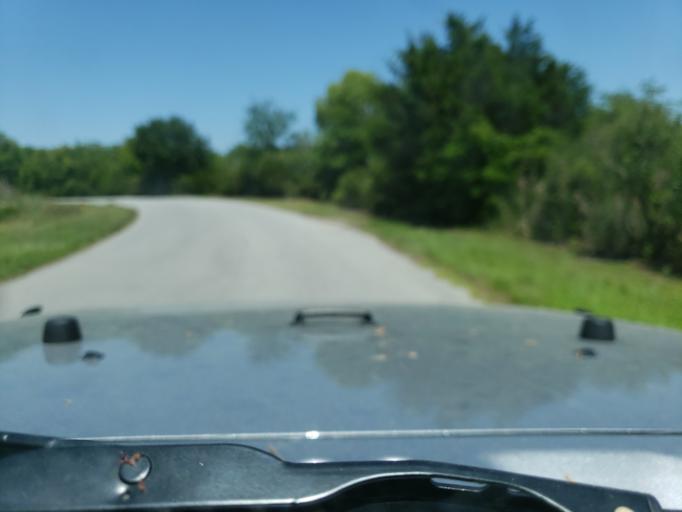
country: US
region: Georgia
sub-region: Chatham County
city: Thunderbolt
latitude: 32.0742
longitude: -81.0450
